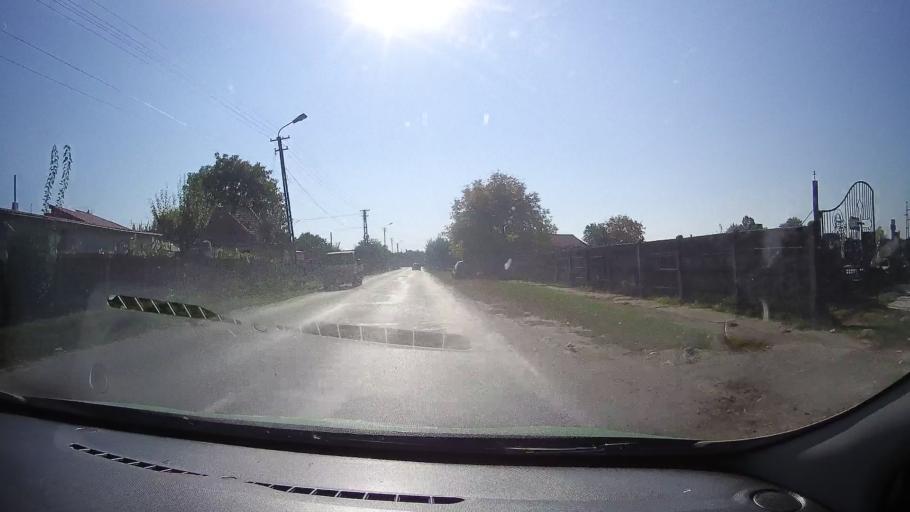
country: RO
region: Satu Mare
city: Carei
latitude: 47.6948
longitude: 22.4726
